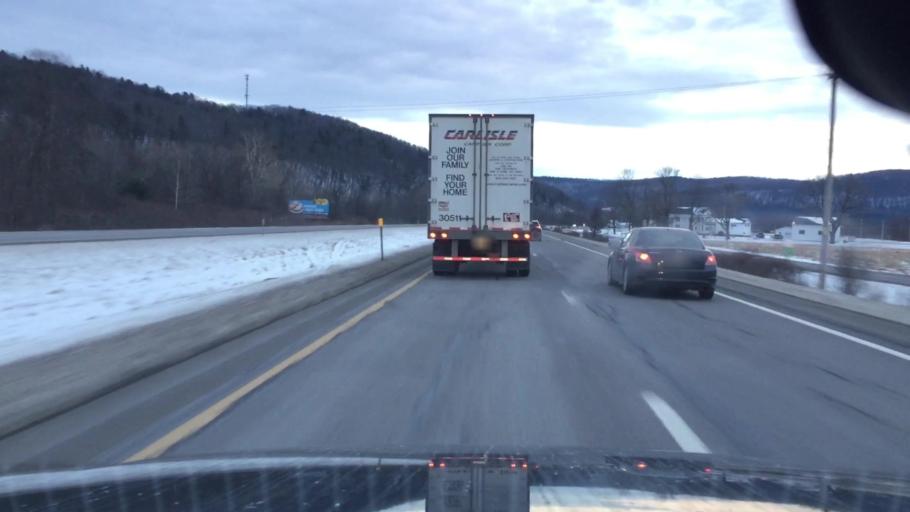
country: US
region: New York
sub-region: Steuben County
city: Gang Mills
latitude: 42.2027
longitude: -77.1662
